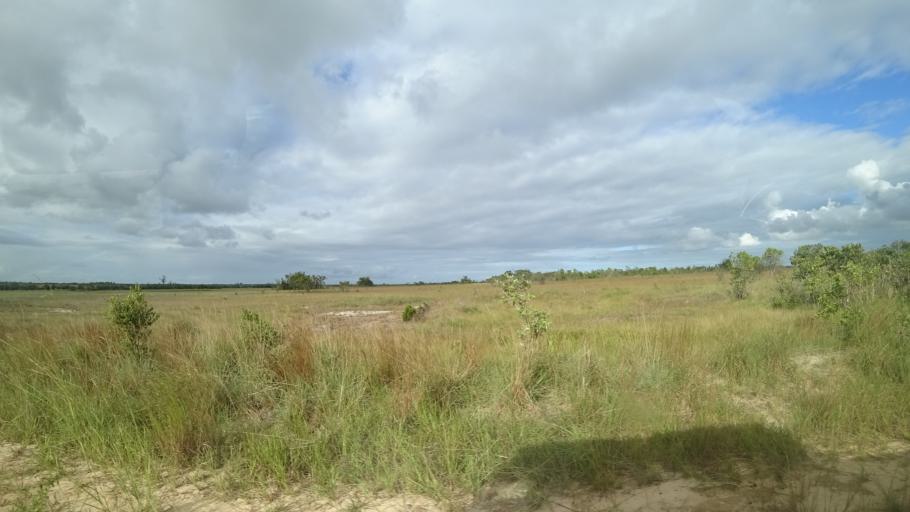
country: MZ
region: Sofala
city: Beira
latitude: -19.6319
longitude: 35.0601
